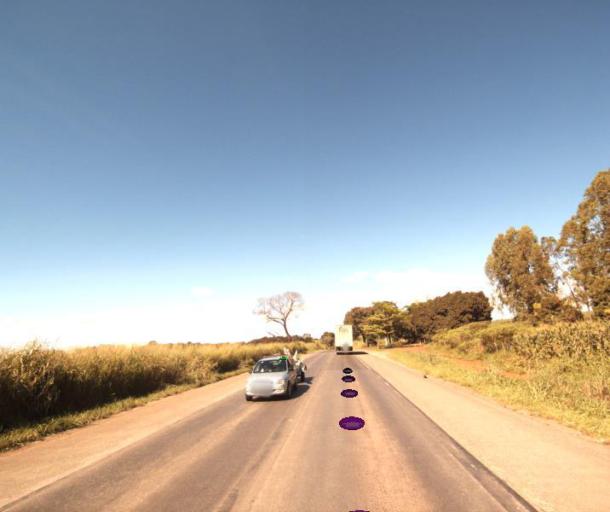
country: BR
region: Goias
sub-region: Itapaci
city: Itapaci
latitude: -15.0579
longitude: -49.4495
